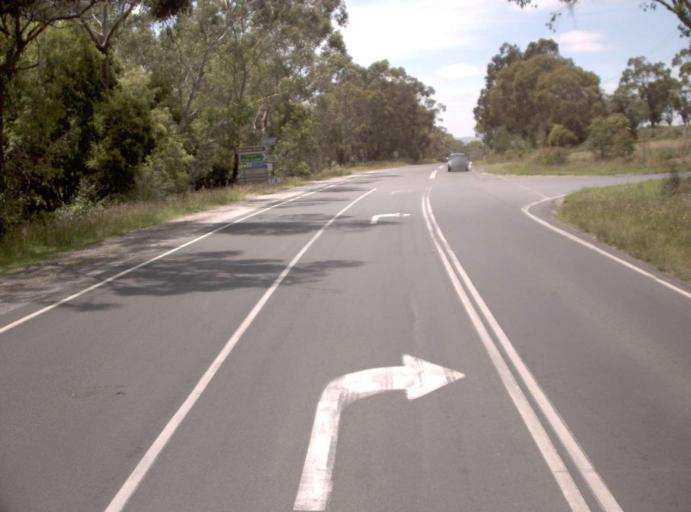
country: AU
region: Victoria
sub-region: Bass Coast
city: North Wonthaggi
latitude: -38.5764
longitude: 146.0233
